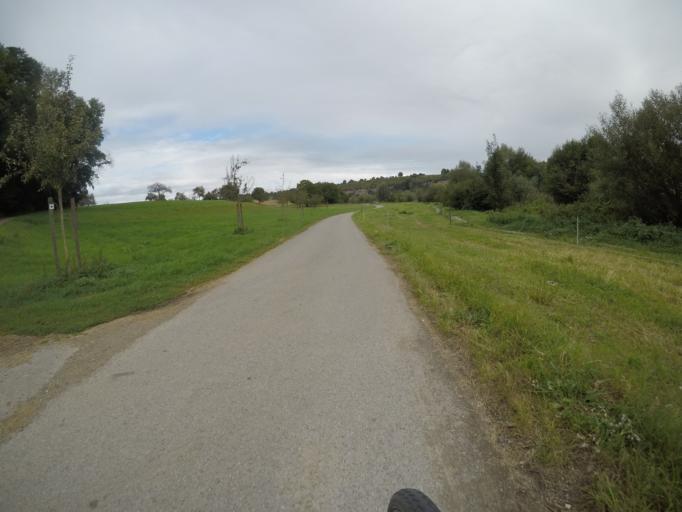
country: DE
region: Baden-Wuerttemberg
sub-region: Regierungsbezirk Stuttgart
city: Marbach am Neckar
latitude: 48.9056
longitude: 9.2569
